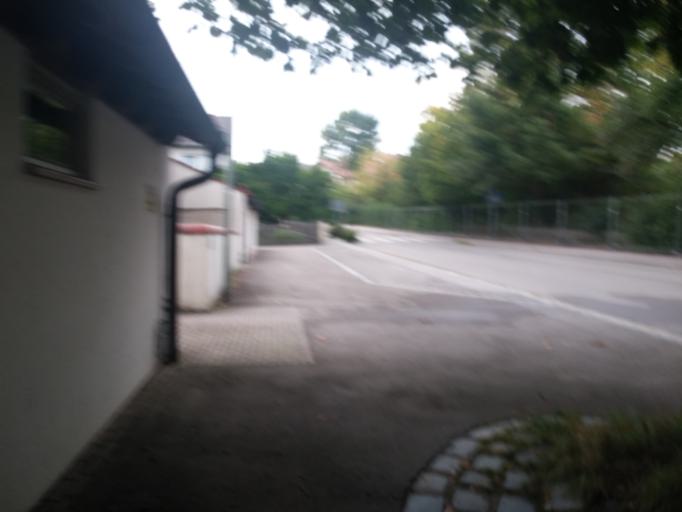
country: DE
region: Bavaria
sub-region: Upper Bavaria
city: Schondorf am Ammersee
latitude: 48.0506
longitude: 11.0888
